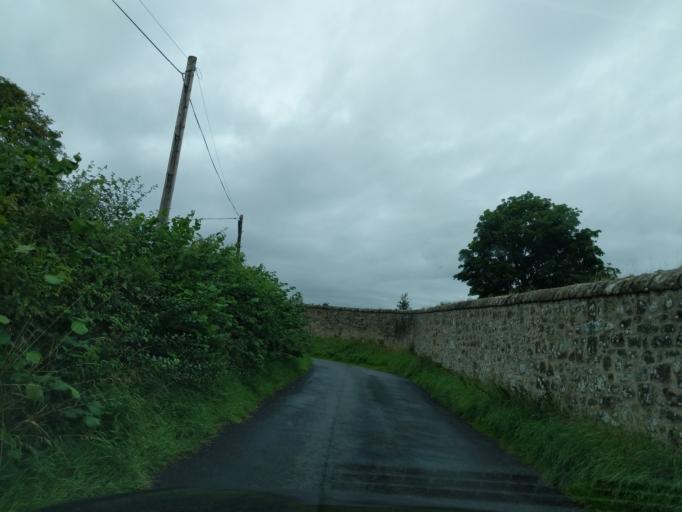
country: GB
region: Scotland
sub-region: Fife
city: Limekilns
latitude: 55.9940
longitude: -3.4730
